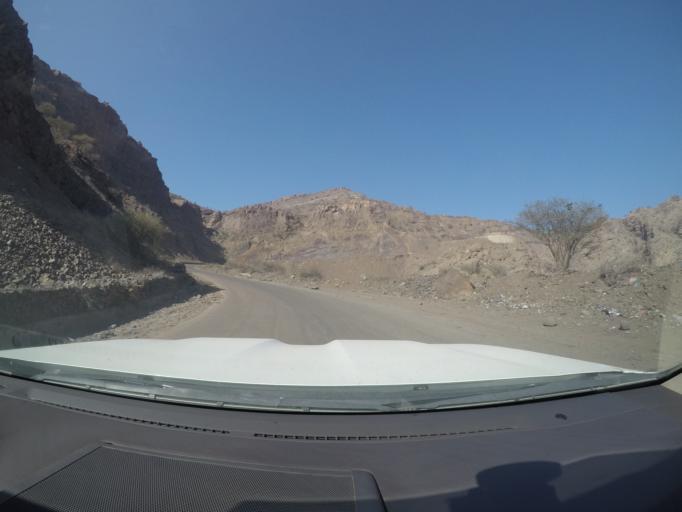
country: YE
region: Ad Dali'
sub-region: Ad Dhale'e
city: Dhalie
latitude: 13.6703
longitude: 44.7703
